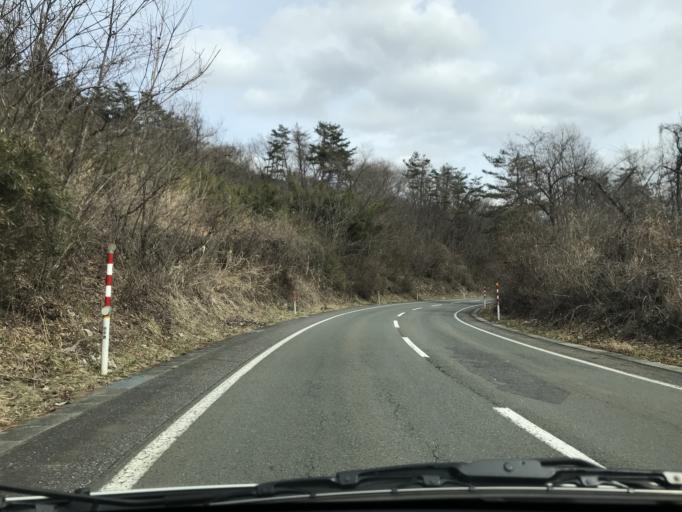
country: JP
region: Iwate
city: Tono
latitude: 39.3022
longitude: 141.3663
